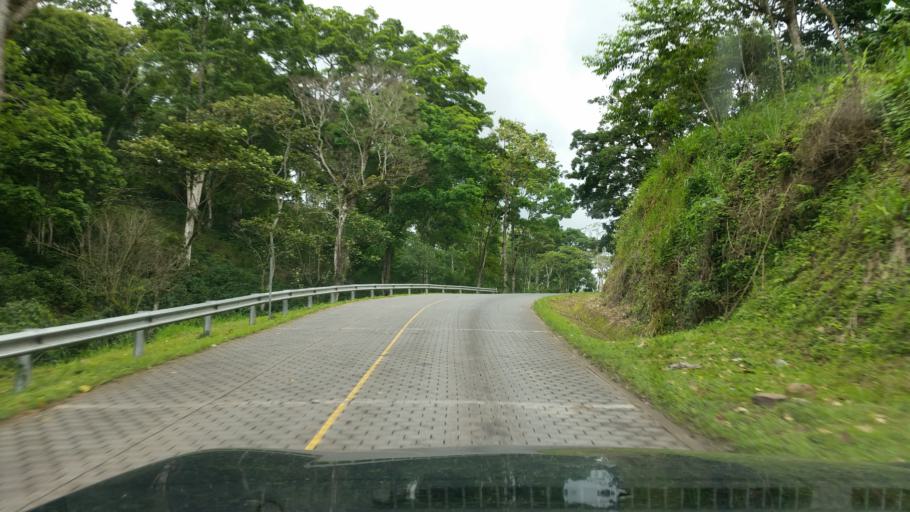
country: NI
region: Jinotega
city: Jinotega
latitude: 13.2025
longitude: -85.7296
